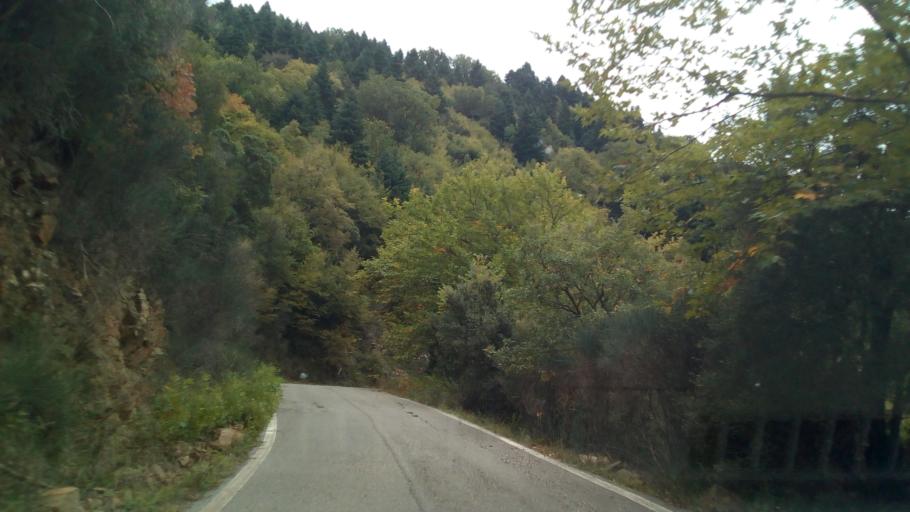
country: GR
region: West Greece
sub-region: Nomos Aitolias kai Akarnanias
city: Thermo
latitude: 38.5903
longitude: 21.8487
